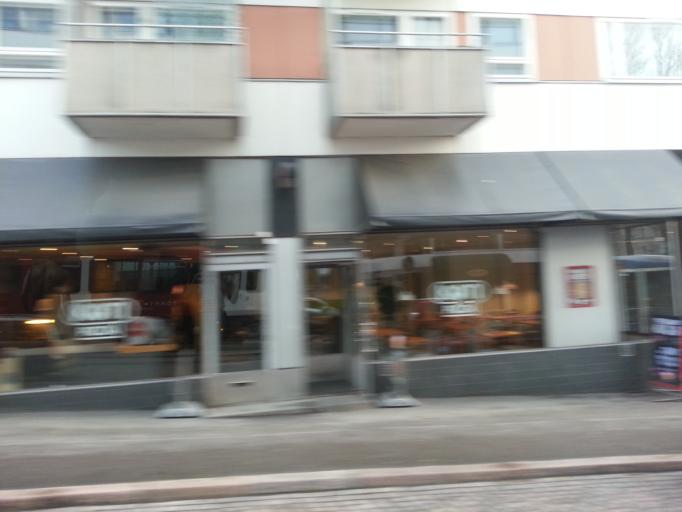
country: FI
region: Uusimaa
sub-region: Helsinki
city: Helsinki
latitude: 60.1830
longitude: 24.9528
